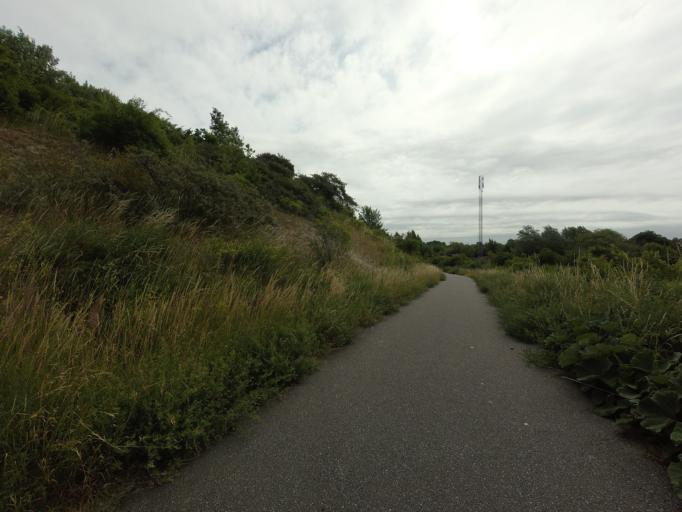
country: SE
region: Skane
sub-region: Malmo
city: Bunkeflostrand
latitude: 55.5627
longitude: 12.9087
